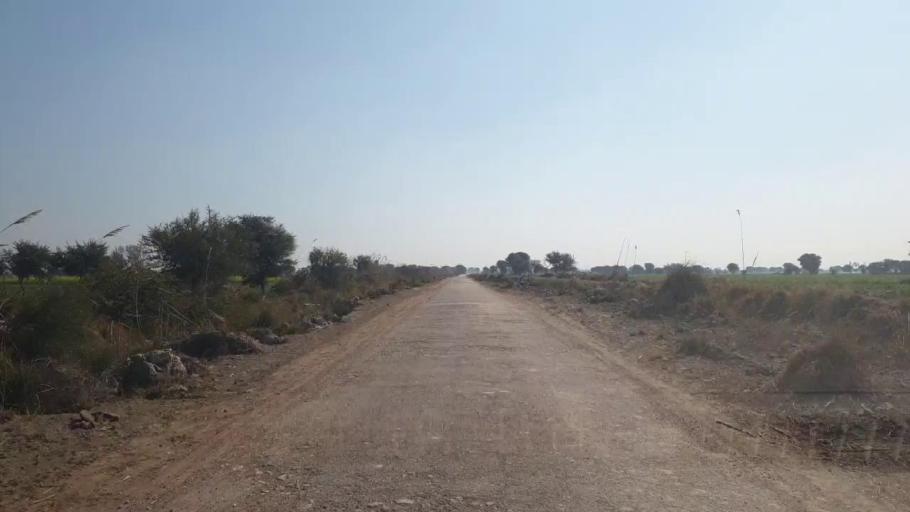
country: PK
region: Sindh
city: Shahdadpur
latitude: 25.9530
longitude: 68.6294
